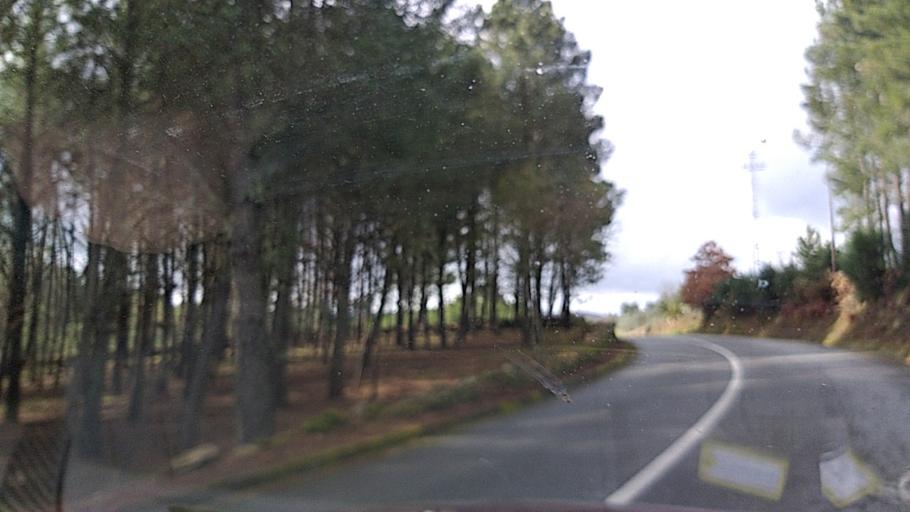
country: PT
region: Guarda
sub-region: Fornos de Algodres
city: Fornos de Algodres
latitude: 40.6612
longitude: -7.5761
